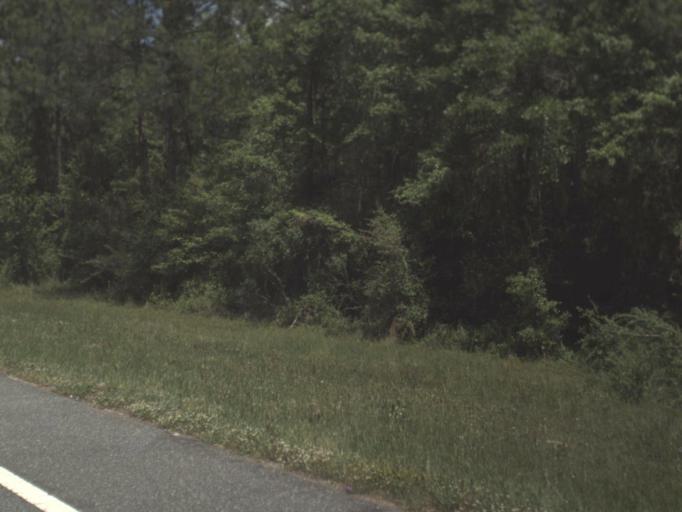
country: US
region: Florida
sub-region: Santa Rosa County
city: Point Baker
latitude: 30.7914
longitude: -87.0414
